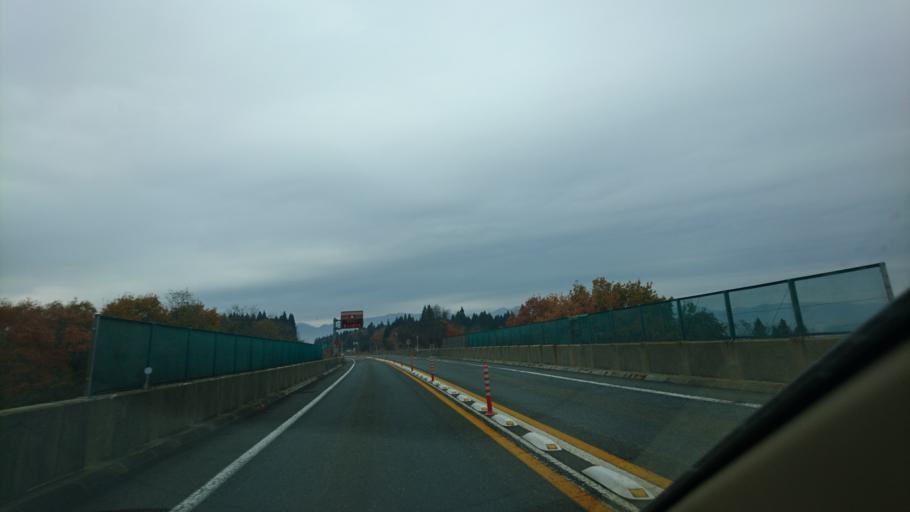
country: JP
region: Iwate
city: Kitakami
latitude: 39.2887
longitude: 140.9913
